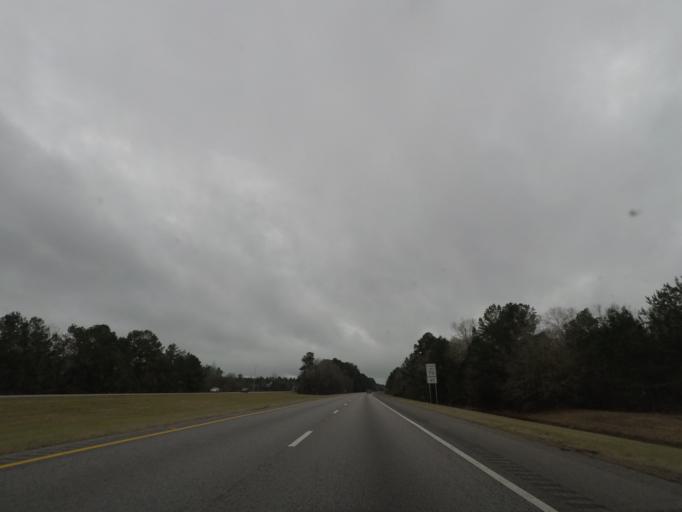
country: US
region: South Carolina
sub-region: Orangeburg County
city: Holly Hill
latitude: 33.4499
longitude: -80.4806
